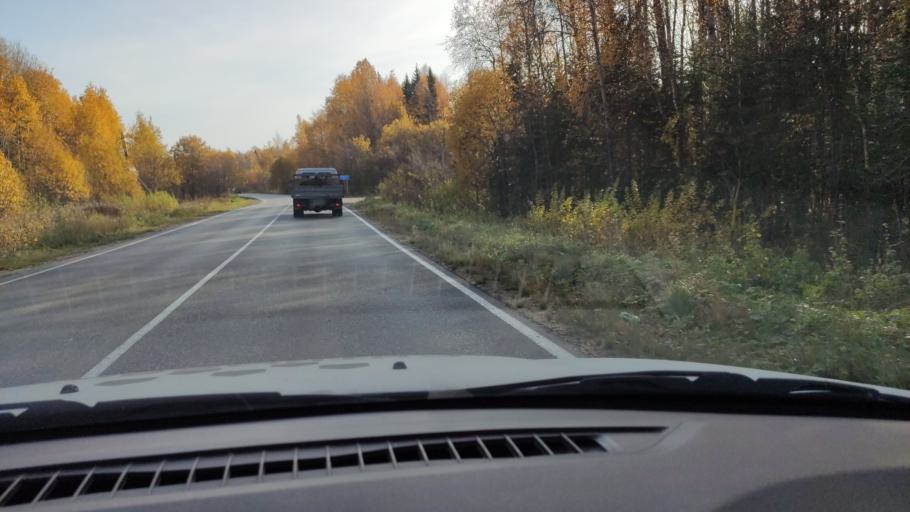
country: RU
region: Perm
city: Novyye Lyady
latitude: 58.0216
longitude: 56.6455
